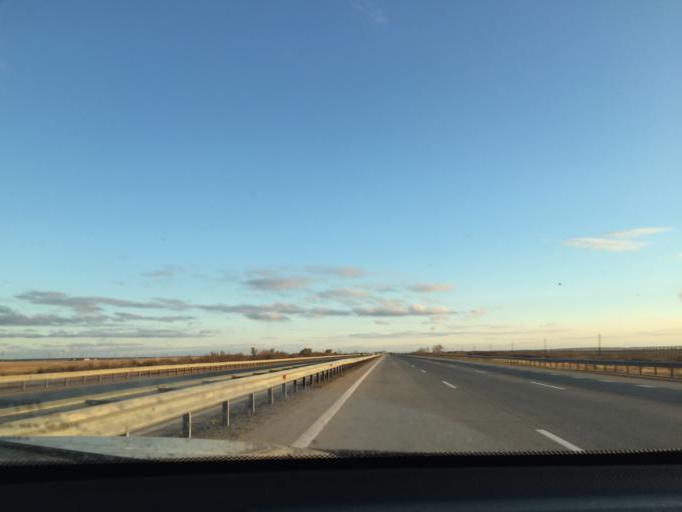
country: KZ
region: Astana Qalasy
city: Astana
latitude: 51.2882
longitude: 71.3603
